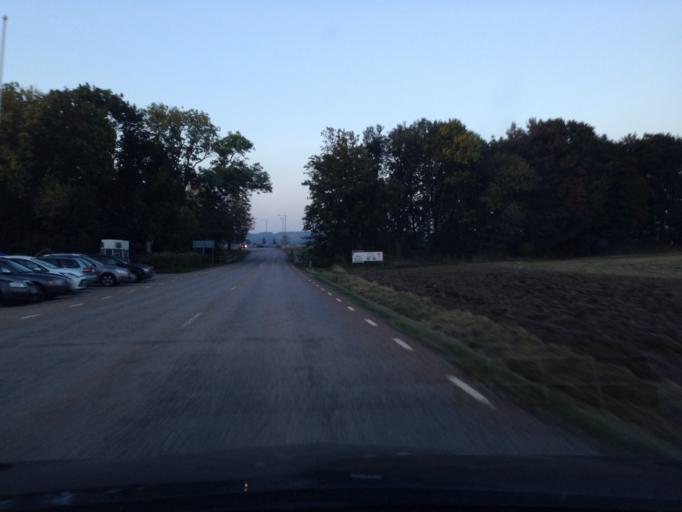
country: SE
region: Skane
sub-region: Bastads Kommun
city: Forslov
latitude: 56.3169
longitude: 12.8875
